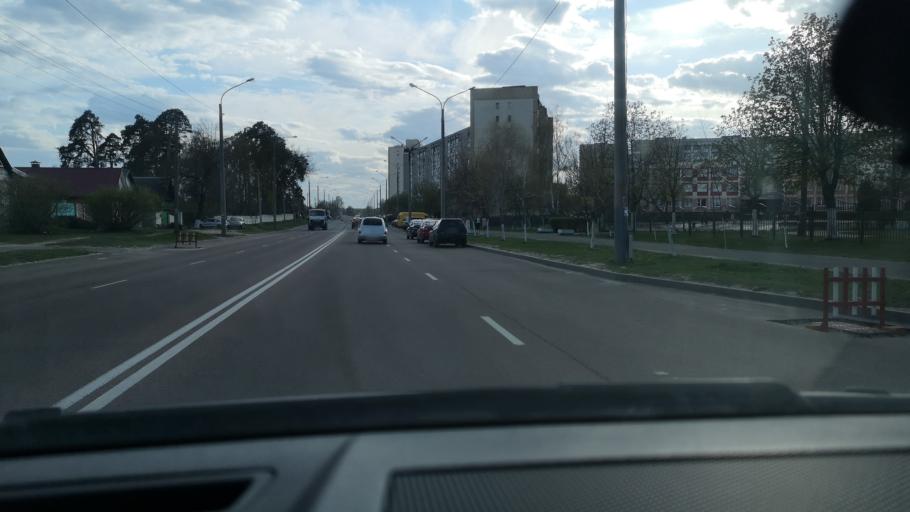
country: BY
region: Gomel
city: Gomel
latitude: 52.4022
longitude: 30.9291
